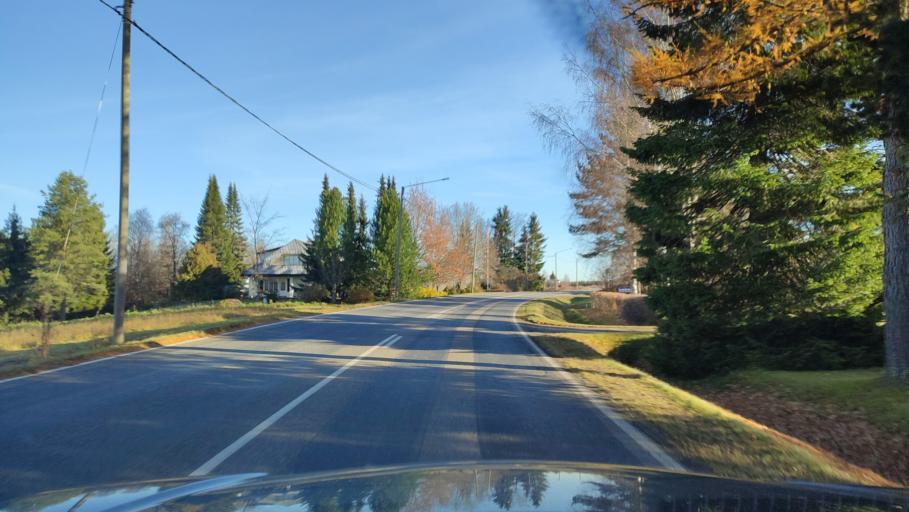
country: FI
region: Southern Ostrobothnia
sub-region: Suupohja
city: Karijoki
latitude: 62.2334
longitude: 21.6538
